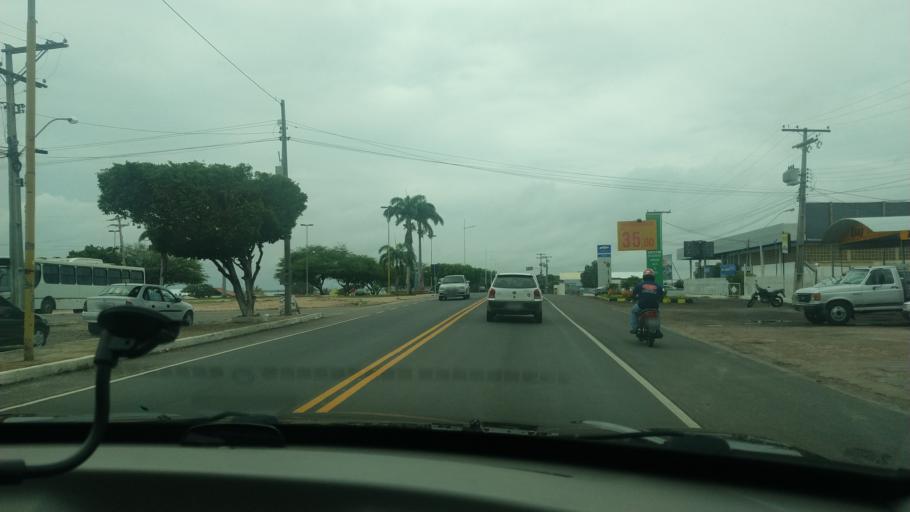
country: BR
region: Bahia
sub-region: Paulo Afonso
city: Paulo Afonso
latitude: -9.4097
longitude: -38.2360
